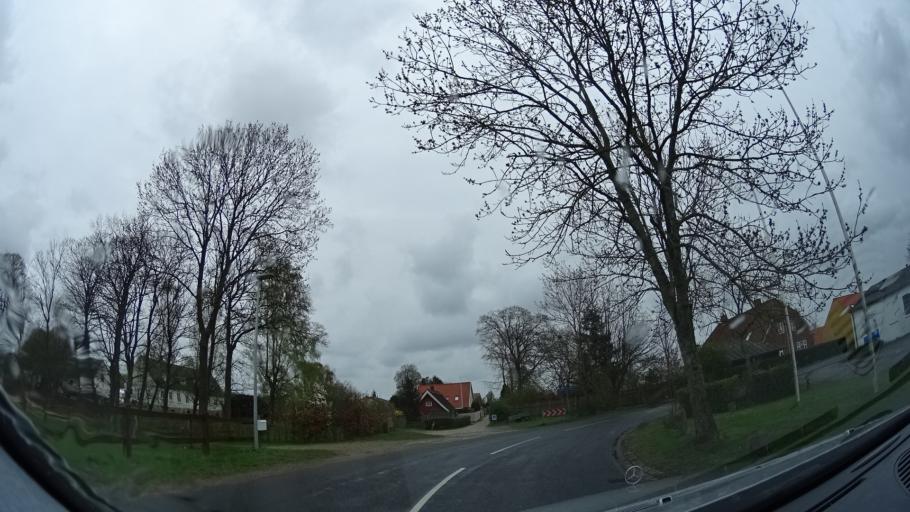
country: DK
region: Zealand
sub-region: Holbaek Kommune
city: Vipperod
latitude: 55.7046
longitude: 11.7765
